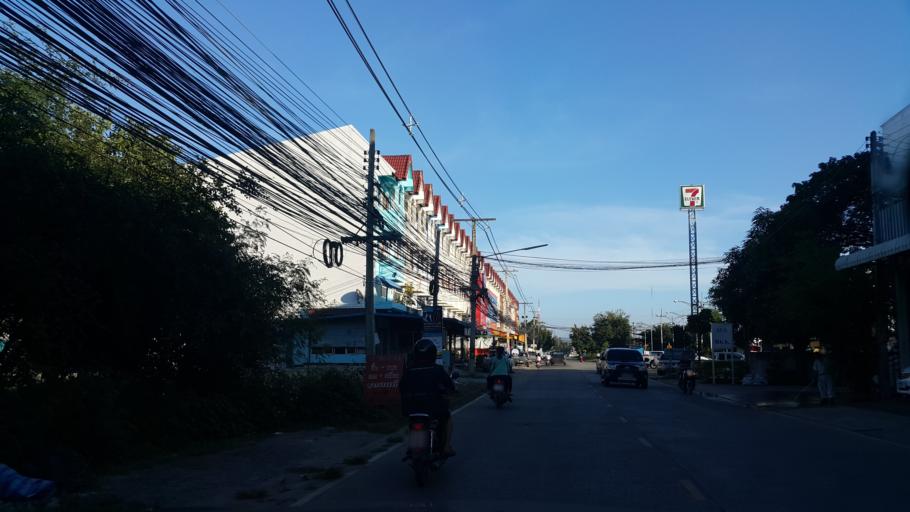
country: TH
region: Lamphun
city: Lamphun
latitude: 18.5937
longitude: 99.0352
